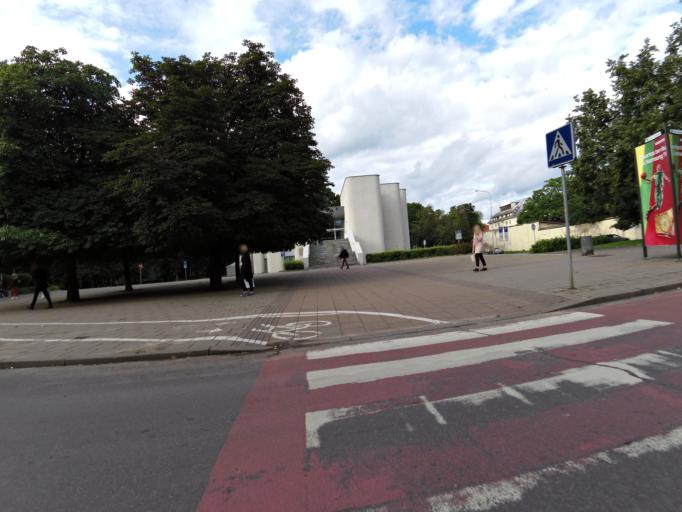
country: LT
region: Vilnius County
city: Naujamiestis
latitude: 54.6825
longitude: 25.2691
